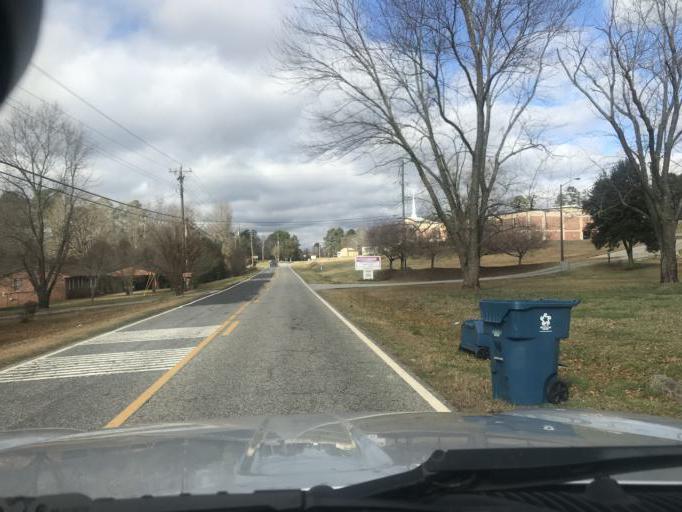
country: US
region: Georgia
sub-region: Barrow County
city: Russell
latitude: 34.0270
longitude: -83.6774
